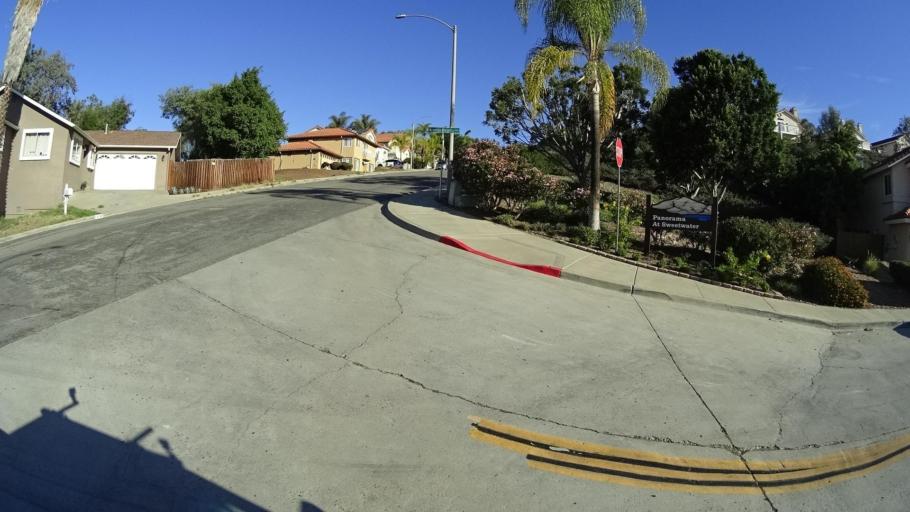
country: US
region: California
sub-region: San Diego County
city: La Presa
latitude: 32.7125
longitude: -116.9887
